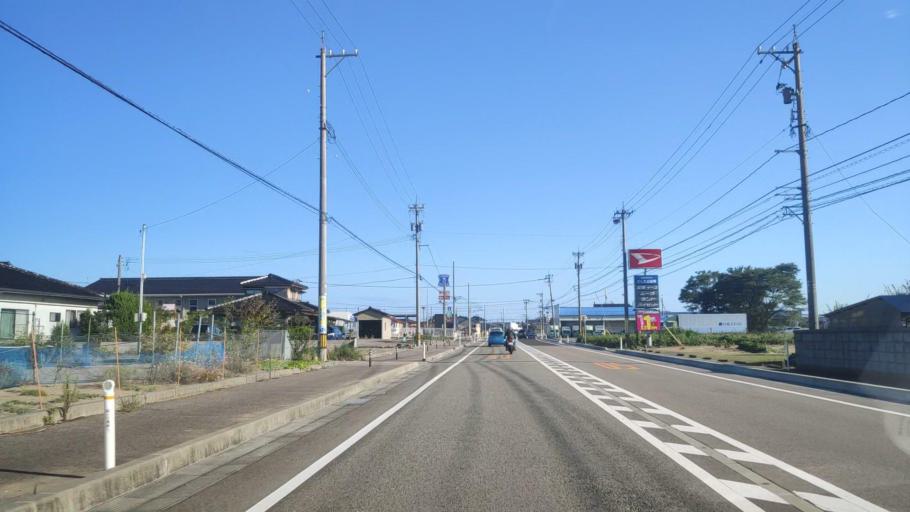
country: JP
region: Ishikawa
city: Tsubata
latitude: 36.7282
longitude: 136.6987
